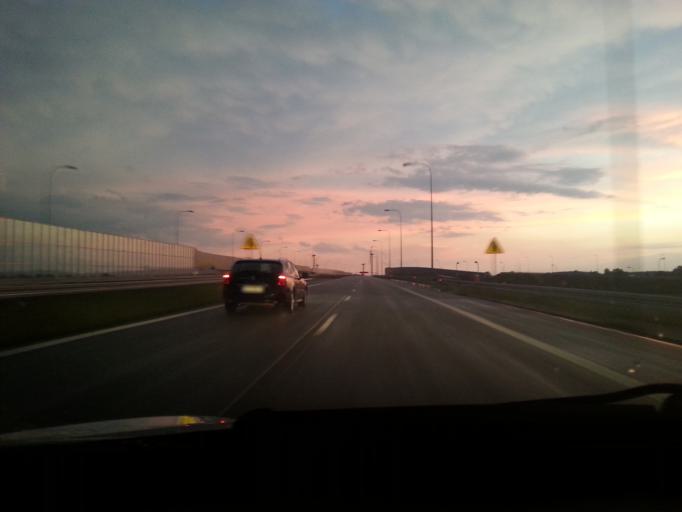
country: PL
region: Lodz Voivodeship
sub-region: Powiat laski
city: Sedziejowice
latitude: 51.5600
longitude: 19.0277
